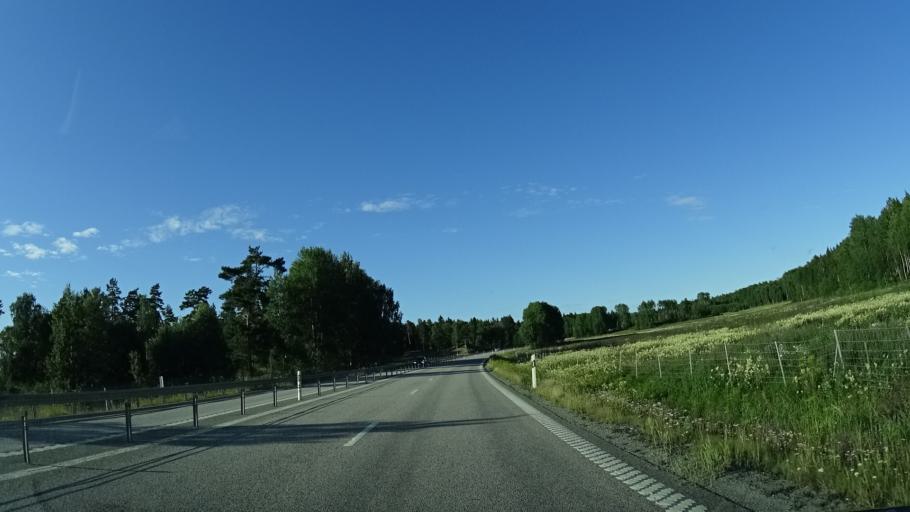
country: SE
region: Stockholm
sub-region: Vallentuna Kommun
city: Vallentuna
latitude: 59.5292
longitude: 18.1904
